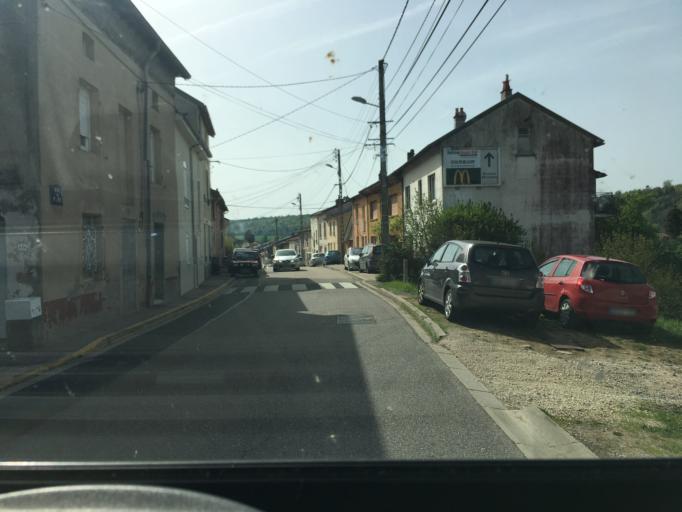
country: FR
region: Lorraine
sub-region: Departement de Meurthe-et-Moselle
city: Chaligny
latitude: 48.6371
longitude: 6.0453
